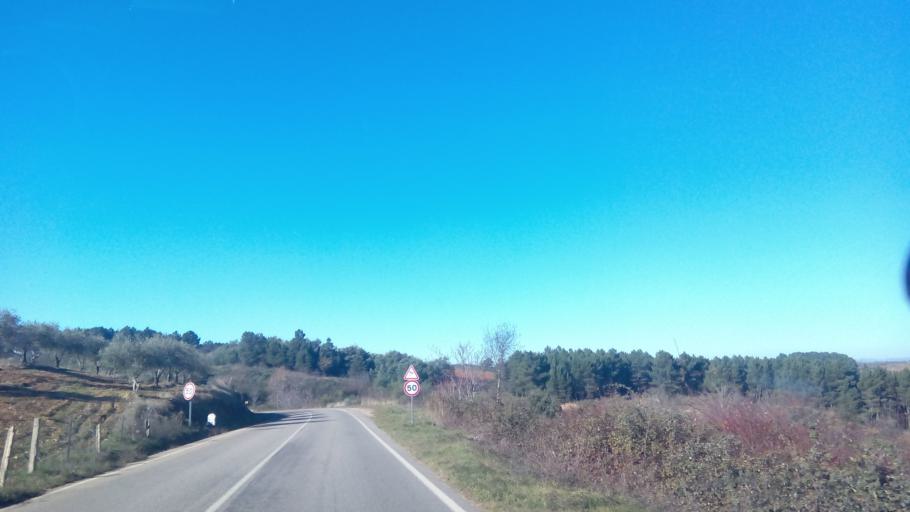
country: PT
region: Braganca
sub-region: Vimioso
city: Vimioso
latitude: 41.6587
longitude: -6.6082
